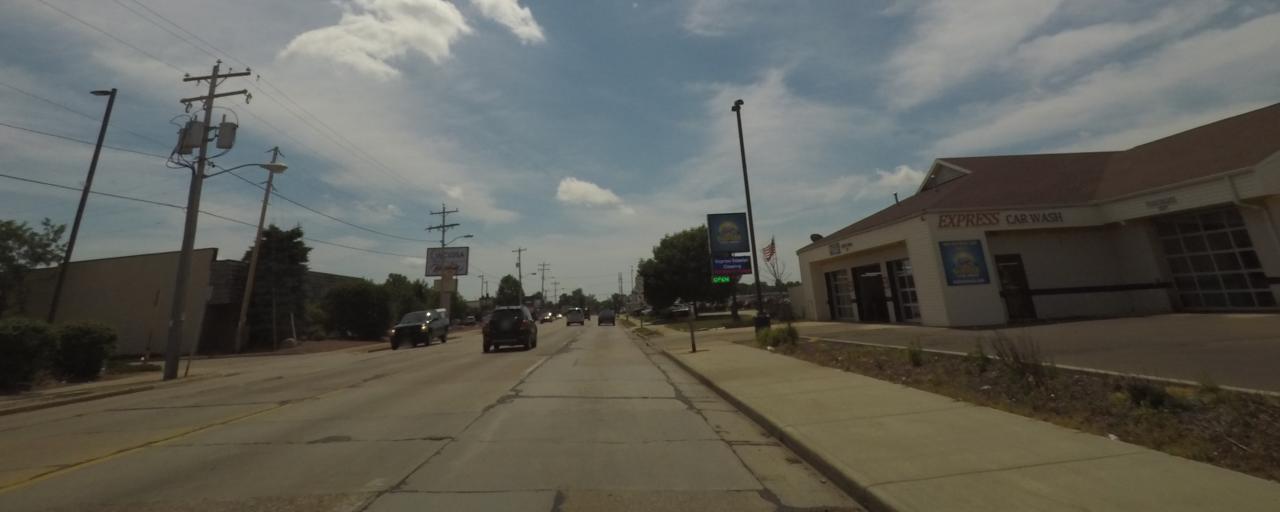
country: US
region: Wisconsin
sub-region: Portage County
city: Whiting
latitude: 44.5009
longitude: -89.5642
